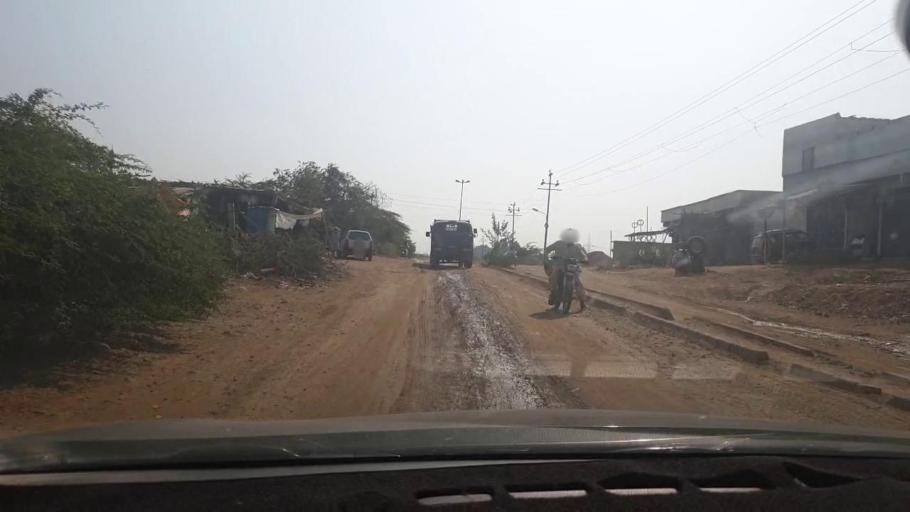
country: PK
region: Sindh
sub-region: Karachi District
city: Karachi
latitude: 25.0010
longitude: 66.9721
